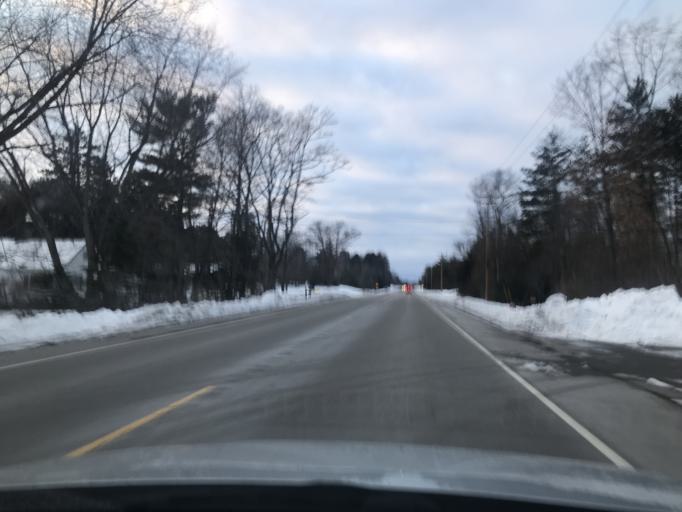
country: US
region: Wisconsin
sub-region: Marinette County
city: Marinette
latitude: 45.1559
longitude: -87.7129
